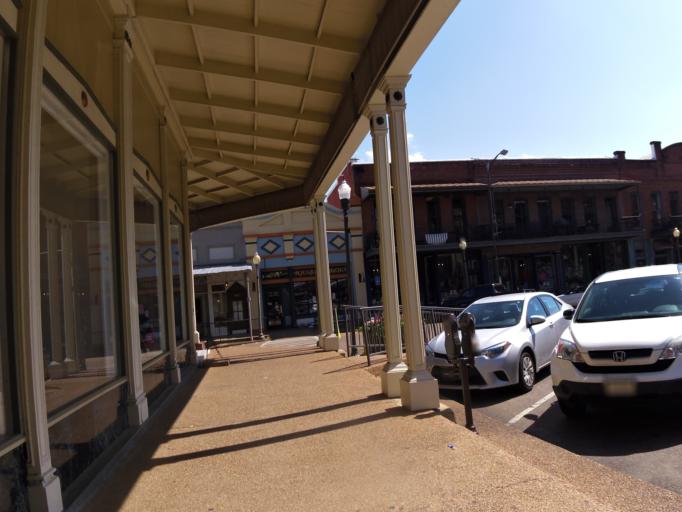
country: US
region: Mississippi
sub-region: Lafayette County
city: Oxford
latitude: 34.3661
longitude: -89.5183
